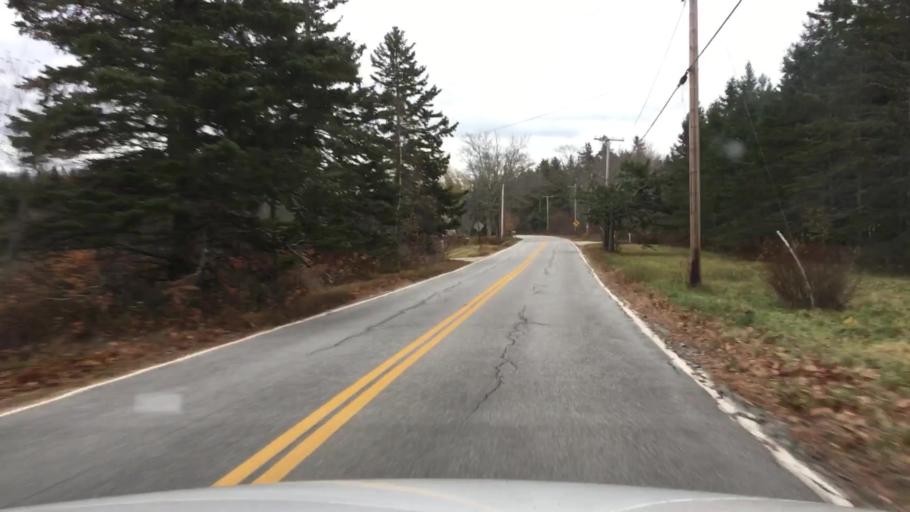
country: US
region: Maine
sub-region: Hancock County
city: Sedgwick
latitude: 44.2770
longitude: -68.5592
